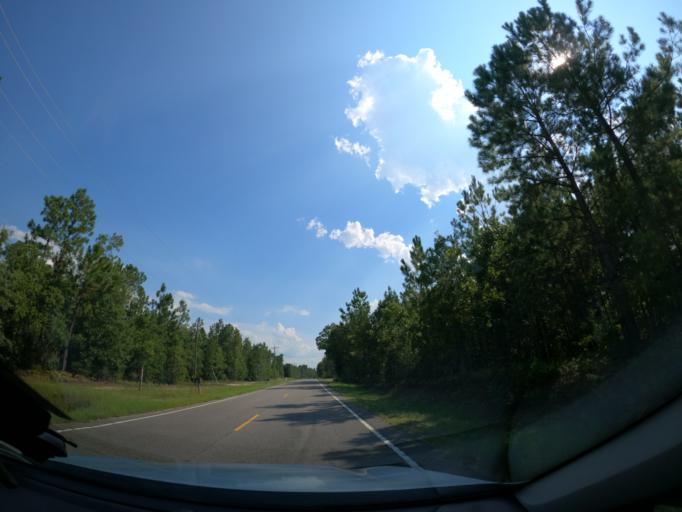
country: US
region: South Carolina
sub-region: Barnwell County
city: Williston
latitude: 33.5304
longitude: -81.4948
